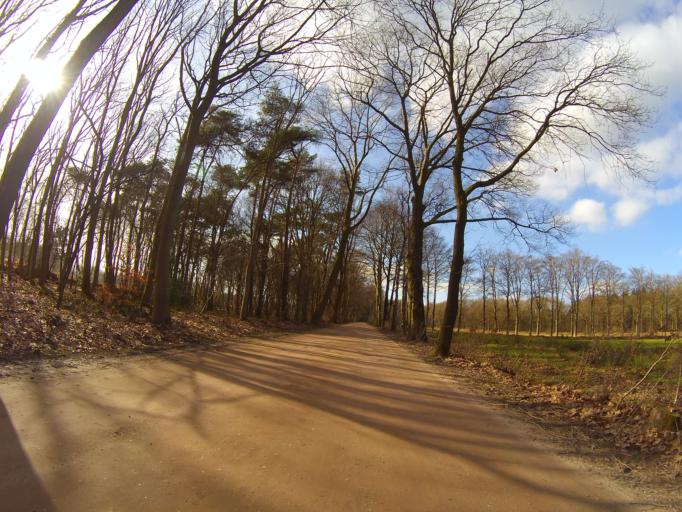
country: NL
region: Gelderland
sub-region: Gemeente Barneveld
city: Barneveld
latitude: 52.1437
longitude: 5.5482
